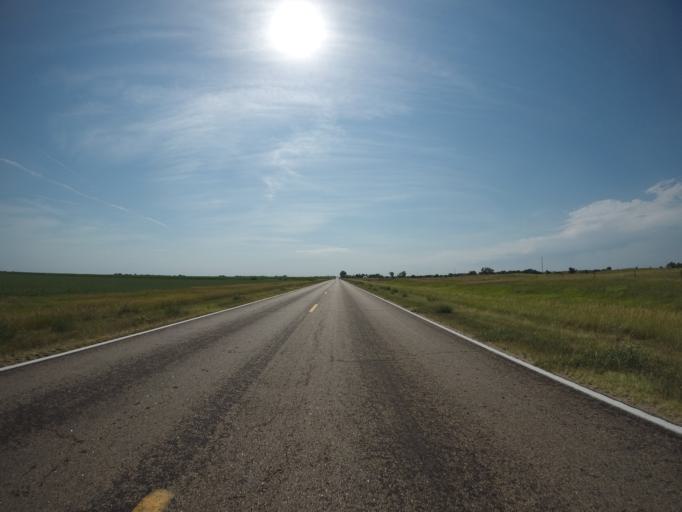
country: US
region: Nebraska
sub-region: Kearney County
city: Minden
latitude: 40.4807
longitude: -98.7493
